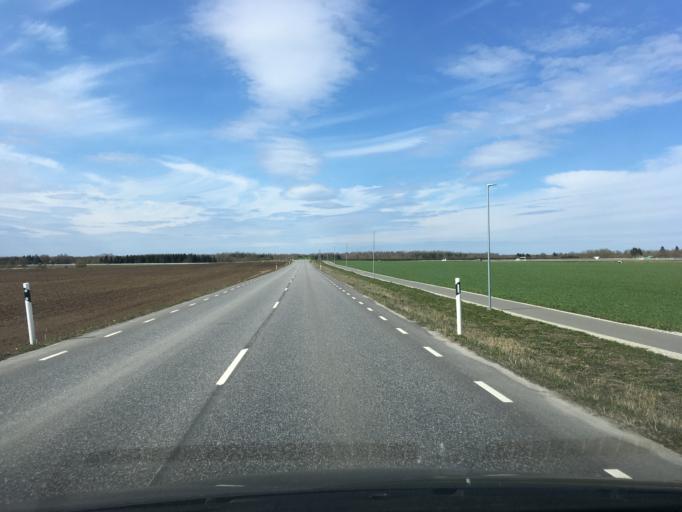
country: EE
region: Harju
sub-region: Maardu linn
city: Maardu
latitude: 59.4465
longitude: 25.0658
